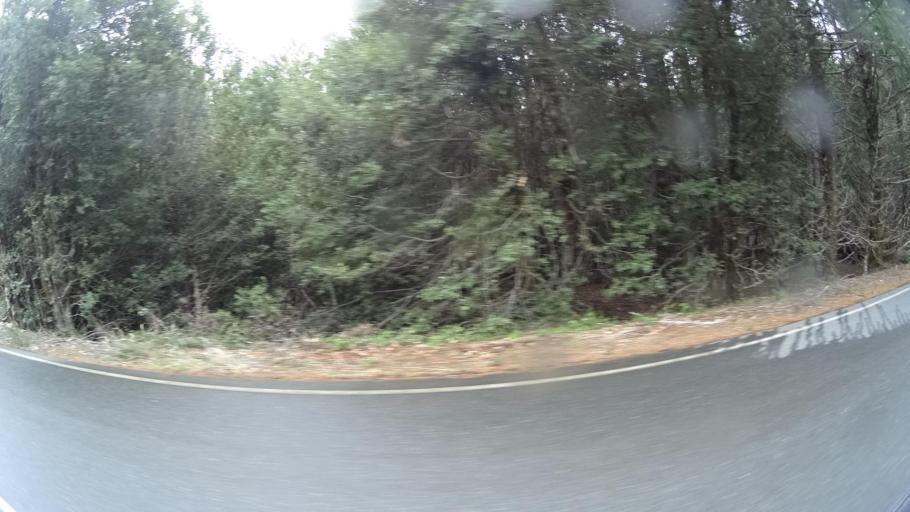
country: US
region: California
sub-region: Humboldt County
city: Willow Creek
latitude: 41.1987
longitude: -123.8058
